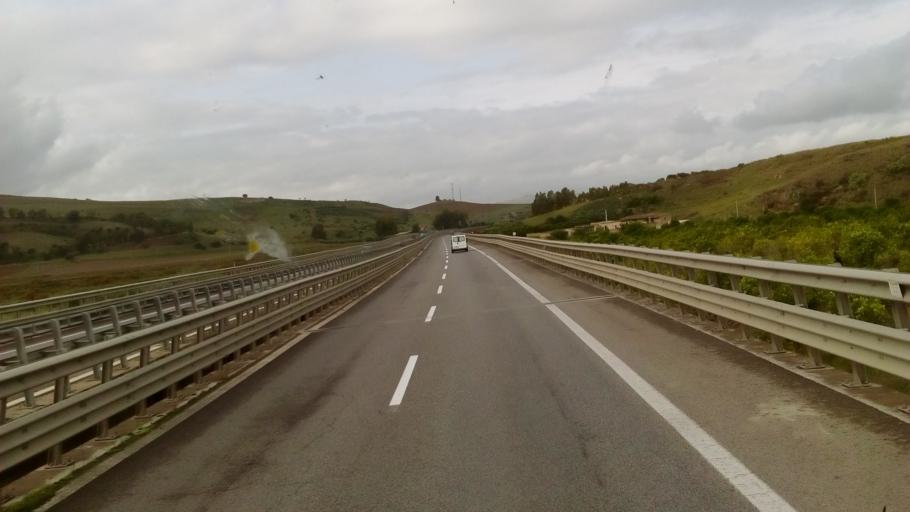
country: IT
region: Sicily
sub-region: Enna
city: Catenanuova
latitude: 37.5609
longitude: 14.6810
